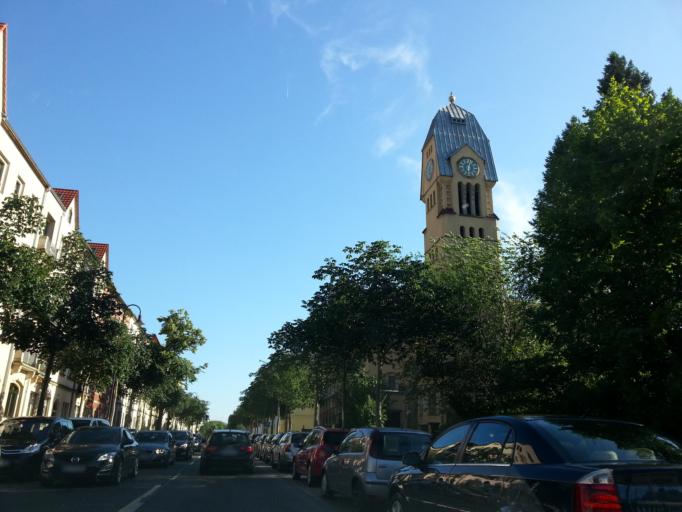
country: DE
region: Saxony
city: Dresden
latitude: 51.0843
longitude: 13.7207
